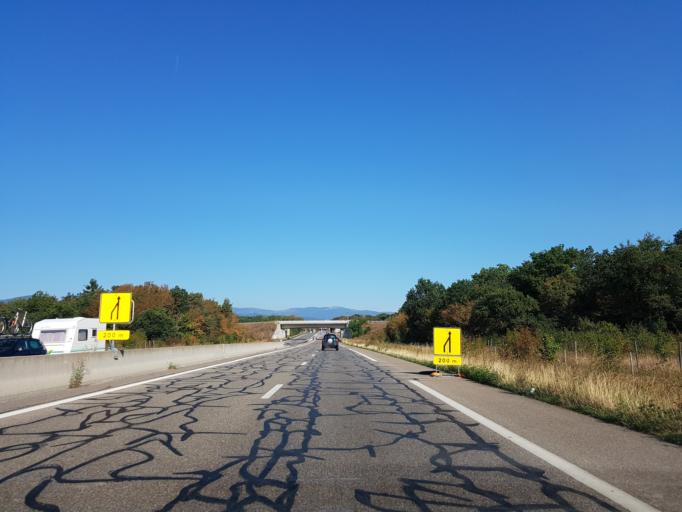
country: FR
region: Alsace
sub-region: Departement du Haut-Rhin
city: Pulversheim
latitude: 47.8176
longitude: 7.2952
